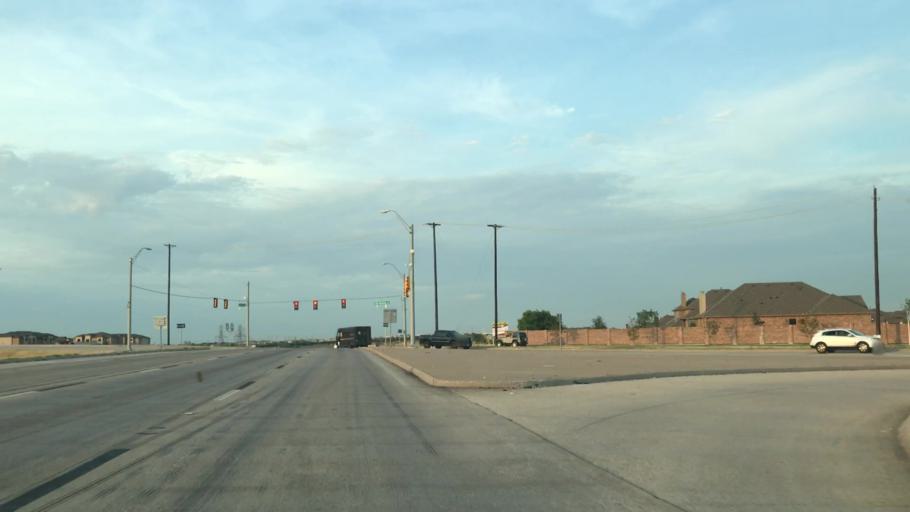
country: US
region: Texas
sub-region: Tarrant County
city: Haslet
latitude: 32.9626
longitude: -97.2991
